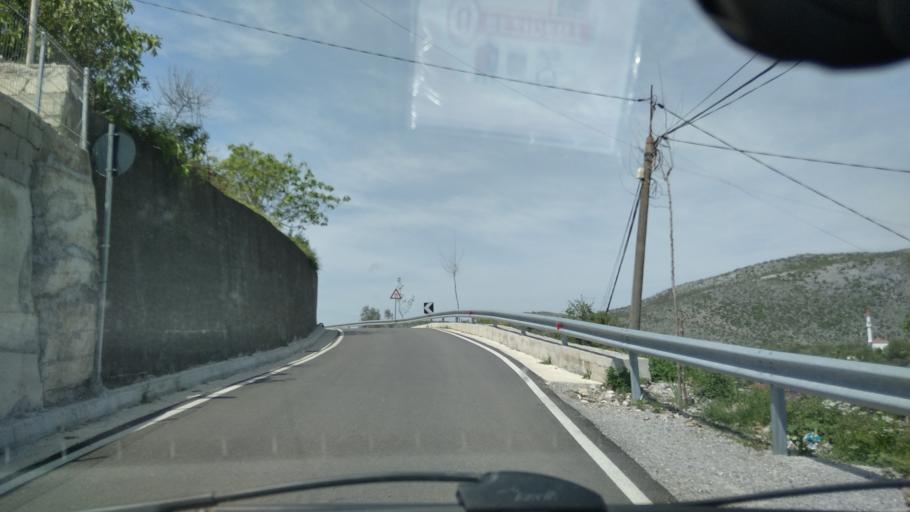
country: AL
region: Shkoder
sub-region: Rrethi i Malesia e Madhe
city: Gruemire
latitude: 42.1237
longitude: 19.5908
